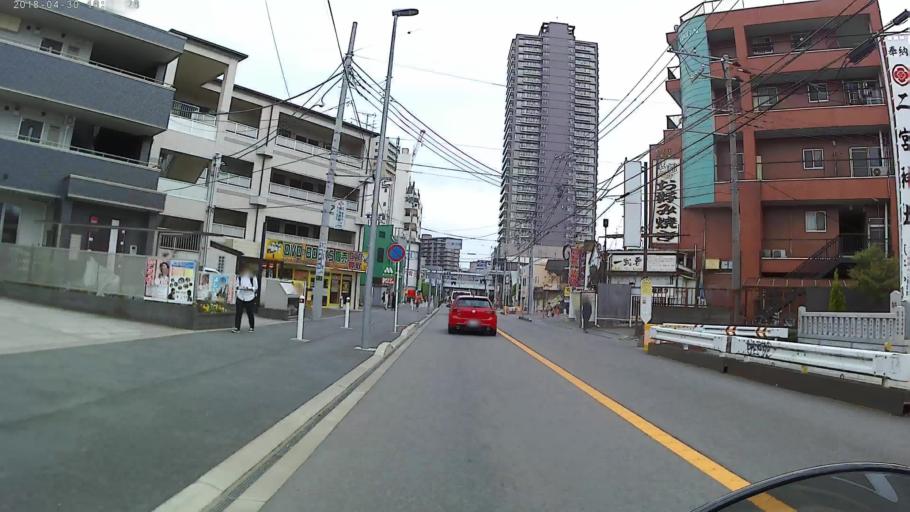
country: JP
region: Tokyo
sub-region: Machida-shi
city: Machida
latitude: 35.5171
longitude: 139.4224
